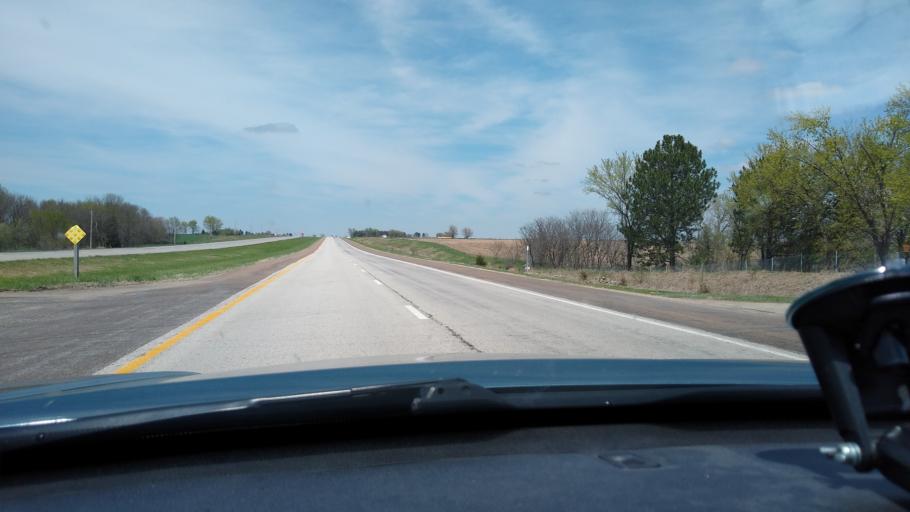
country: US
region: Kansas
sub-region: Republic County
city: Belleville
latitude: 39.7874
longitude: -97.6520
